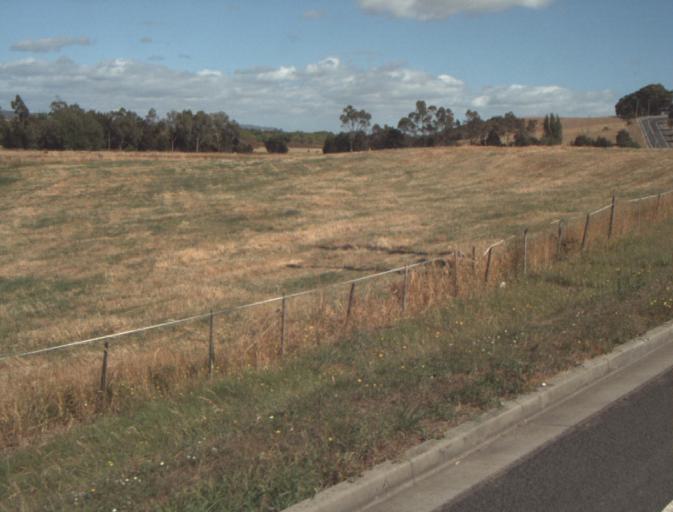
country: AU
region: Tasmania
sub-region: Launceston
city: Newstead
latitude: -41.4347
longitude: 147.1756
